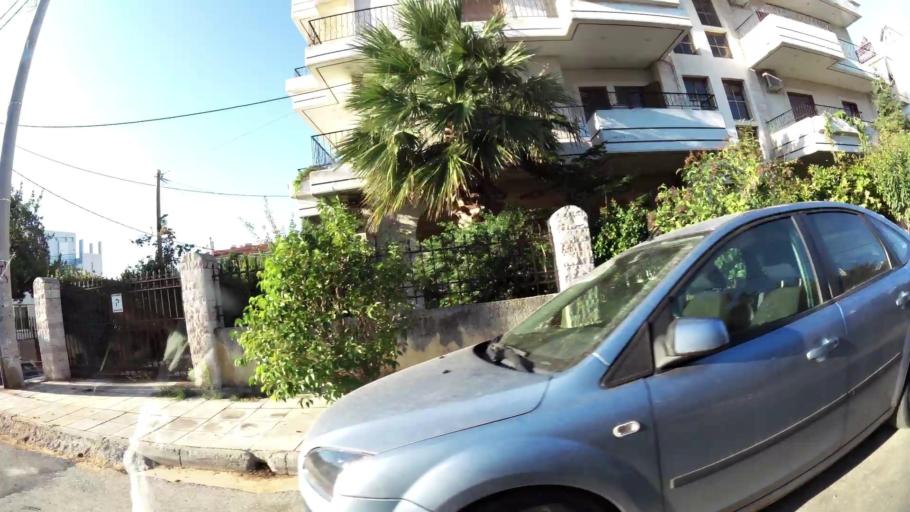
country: GR
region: Attica
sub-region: Nomarchia Athinas
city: Vrilissia
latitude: 38.0352
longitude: 23.8436
